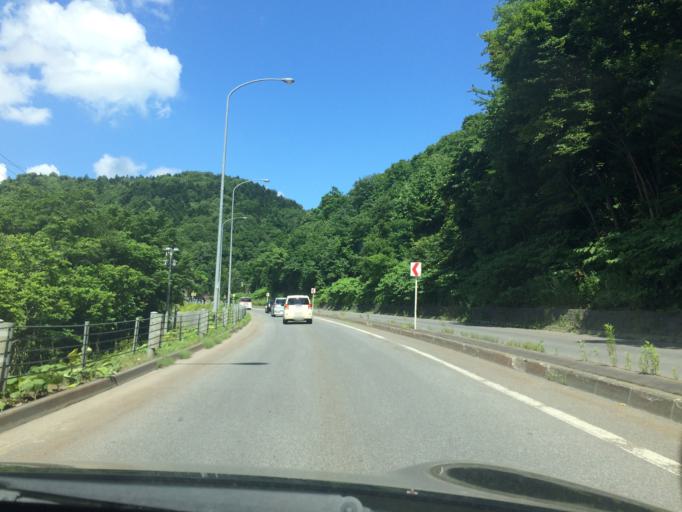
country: JP
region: Hokkaido
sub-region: Asahikawa-shi
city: Asahikawa
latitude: 43.7370
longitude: 142.2413
